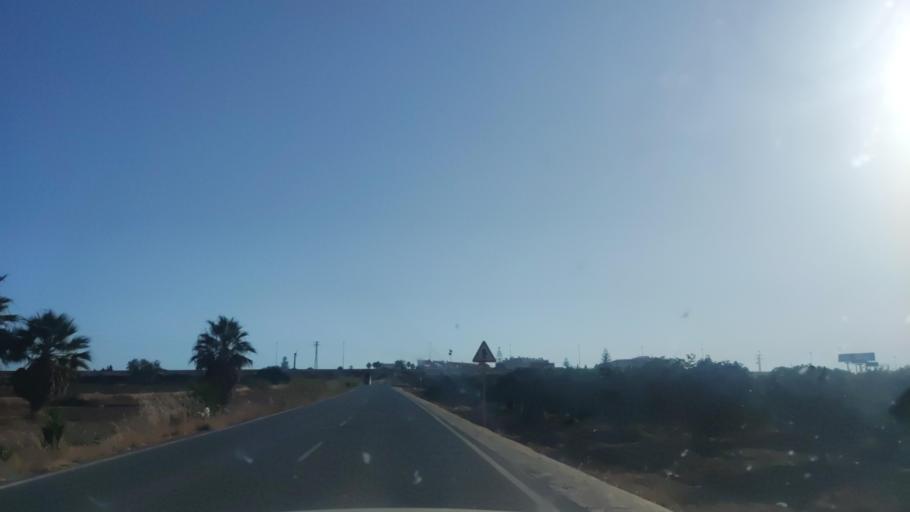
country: ES
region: Murcia
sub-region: Murcia
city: San Javier
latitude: 37.8041
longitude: -0.8603
